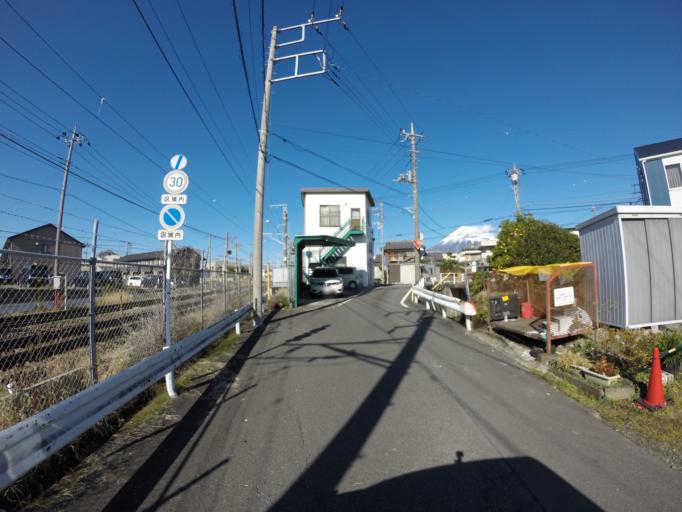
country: JP
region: Shizuoka
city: Fuji
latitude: 35.1794
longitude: 138.6550
